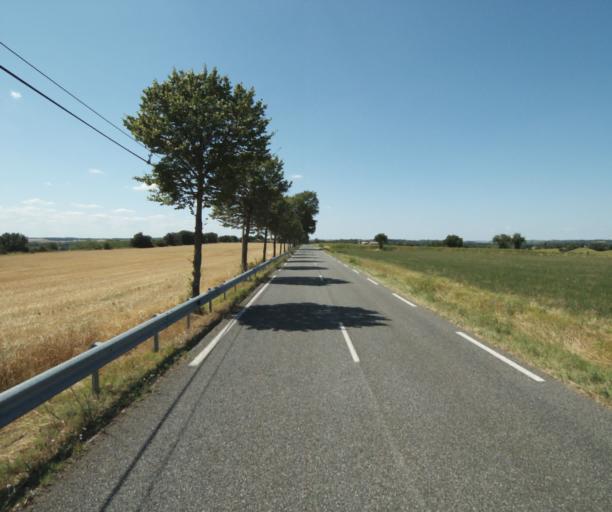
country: FR
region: Midi-Pyrenees
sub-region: Departement de la Haute-Garonne
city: Saint-Felix-Lauragais
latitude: 43.5016
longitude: 1.8786
